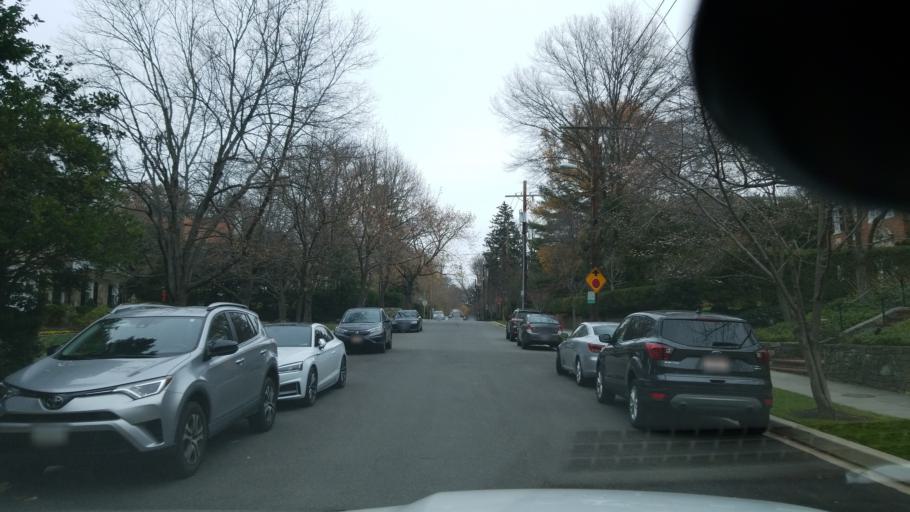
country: US
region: Maryland
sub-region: Montgomery County
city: Friendship Village
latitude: 38.9280
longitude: -77.0864
